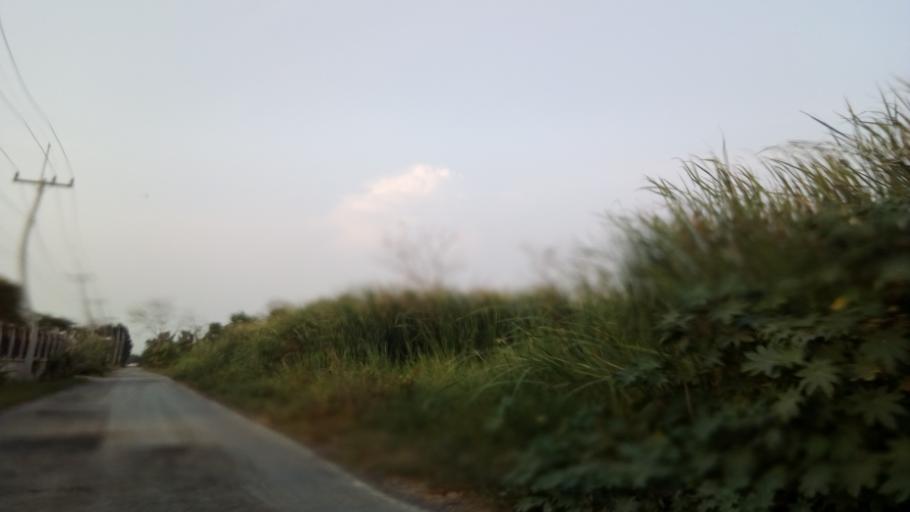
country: TH
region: Pathum Thani
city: Nong Suea
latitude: 14.0618
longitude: 100.8312
